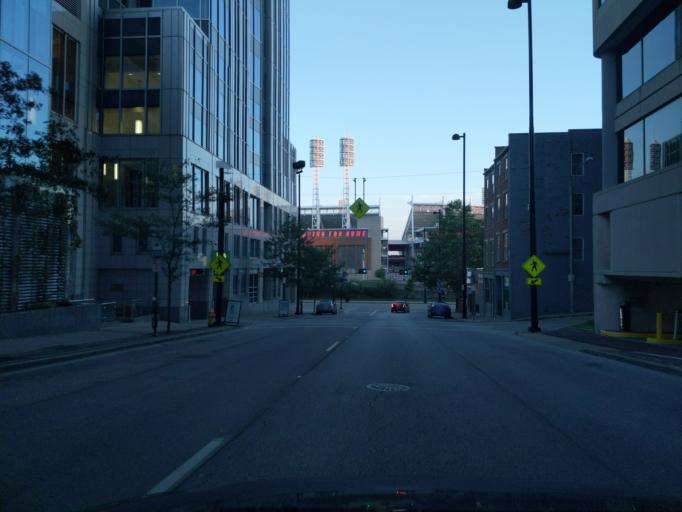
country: US
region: Kentucky
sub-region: Campbell County
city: Newport
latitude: 39.1002
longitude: -84.5077
